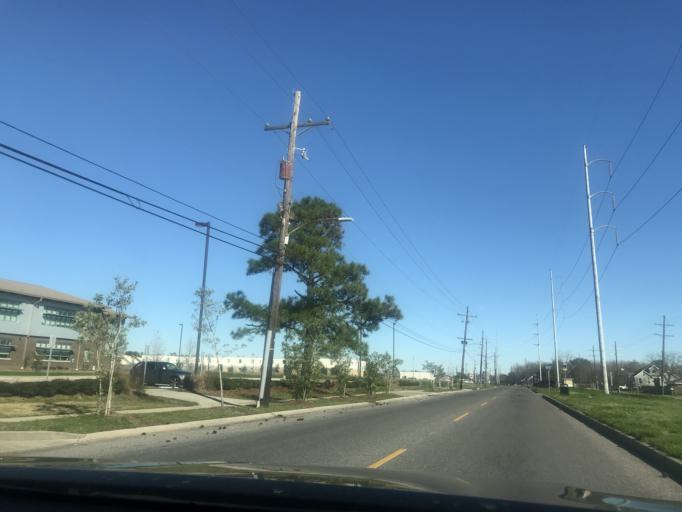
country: US
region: Louisiana
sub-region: Saint Bernard Parish
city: Arabi
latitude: 30.0217
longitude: -90.0025
